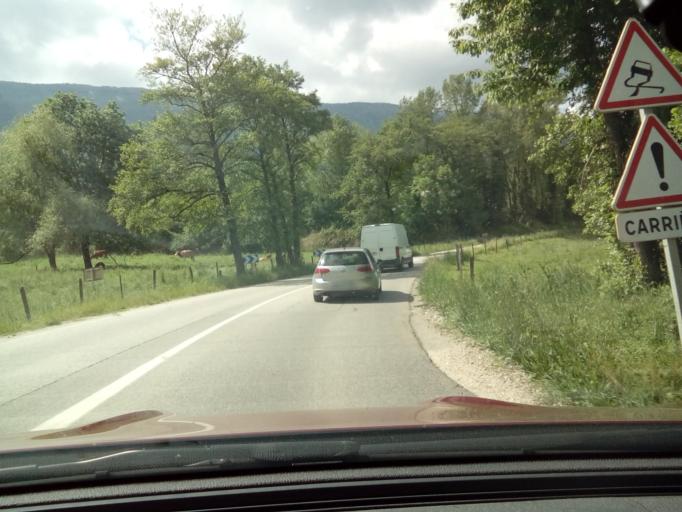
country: FR
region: Rhone-Alpes
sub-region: Departement de la Savoie
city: La Motte-Servolex
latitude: 45.6075
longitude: 5.8607
